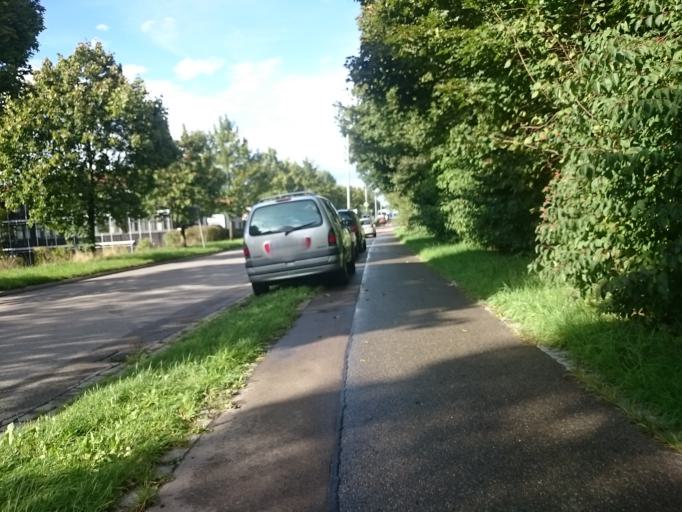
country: DE
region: Bavaria
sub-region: Swabia
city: Lauben
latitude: 47.7565
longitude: 10.3168
